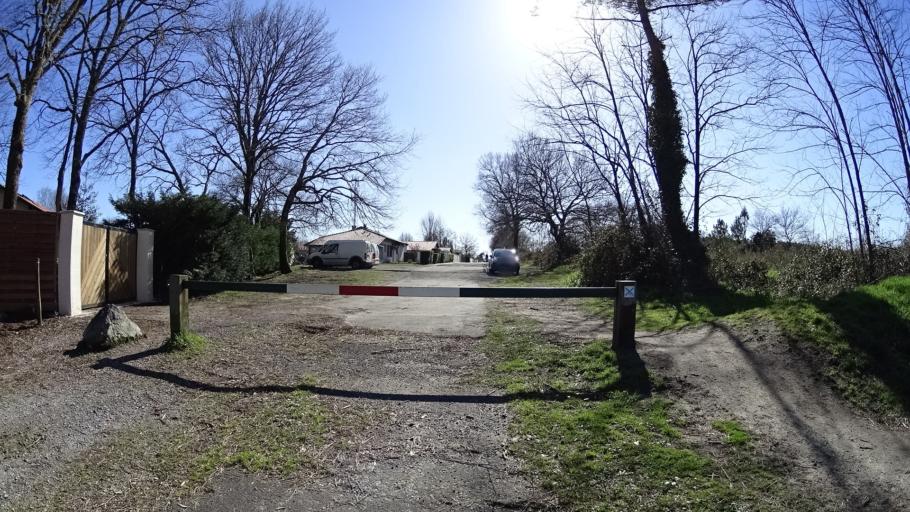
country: FR
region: Aquitaine
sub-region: Departement des Landes
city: Saint-Paul-les-Dax
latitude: 43.7351
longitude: -1.0836
